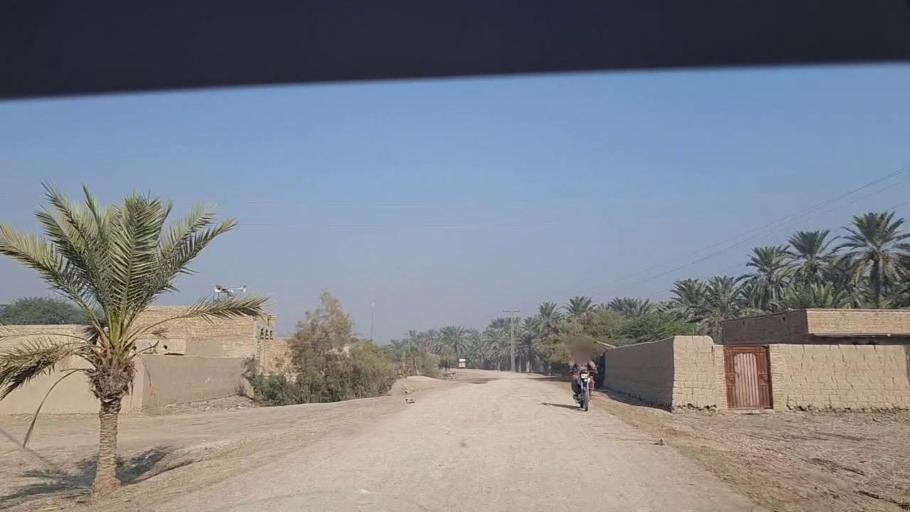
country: PK
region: Sindh
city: Khairpur
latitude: 27.4971
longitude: 68.7371
